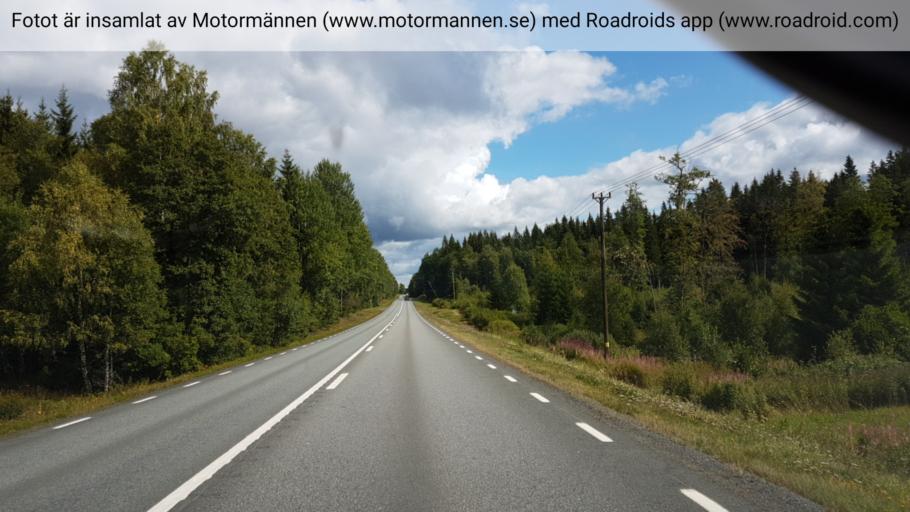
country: SE
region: Joenkoeping
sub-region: Aneby Kommun
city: Hestra
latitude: 57.7737
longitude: 14.5128
